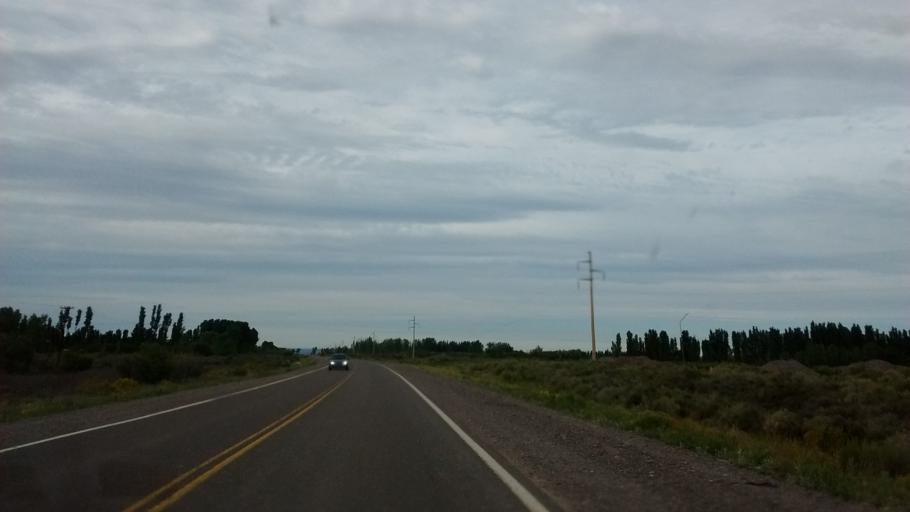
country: AR
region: Rio Negro
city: Catriel
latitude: -37.9029
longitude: -67.8630
